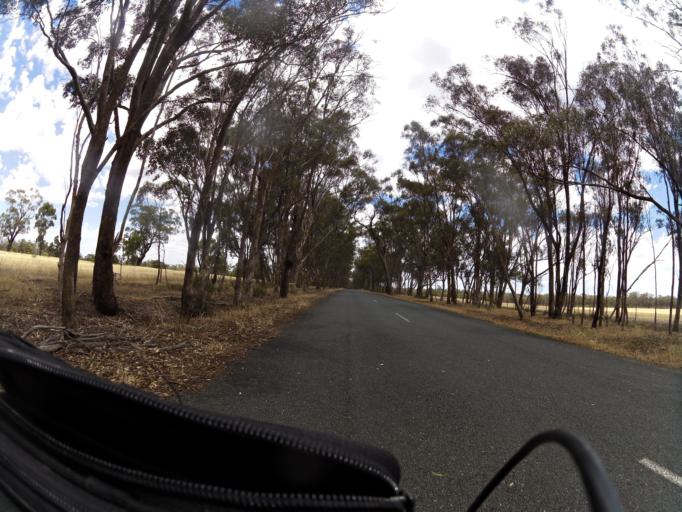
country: AU
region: Victoria
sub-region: Greater Shepparton
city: Shepparton
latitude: -36.6807
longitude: 145.1935
